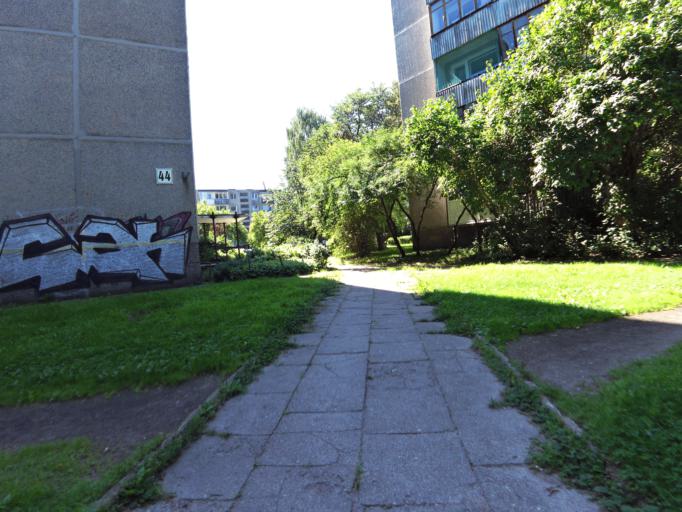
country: LT
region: Vilnius County
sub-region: Vilnius
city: Vilnius
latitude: 54.7038
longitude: 25.2943
